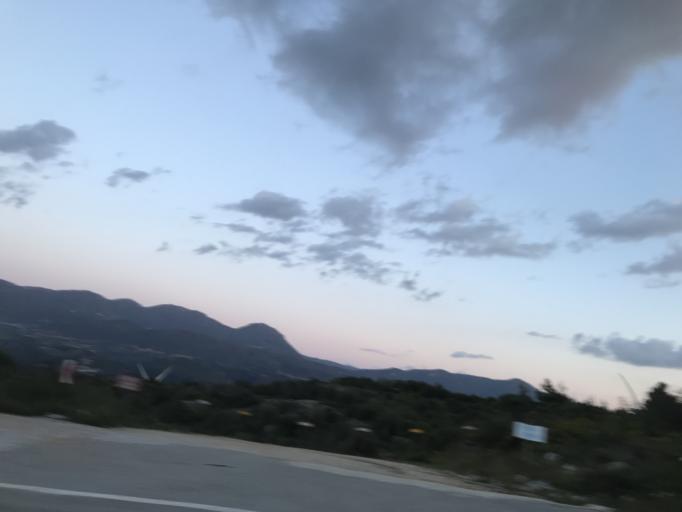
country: TR
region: Hatay
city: Buyukcat
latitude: 36.0943
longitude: 36.0378
